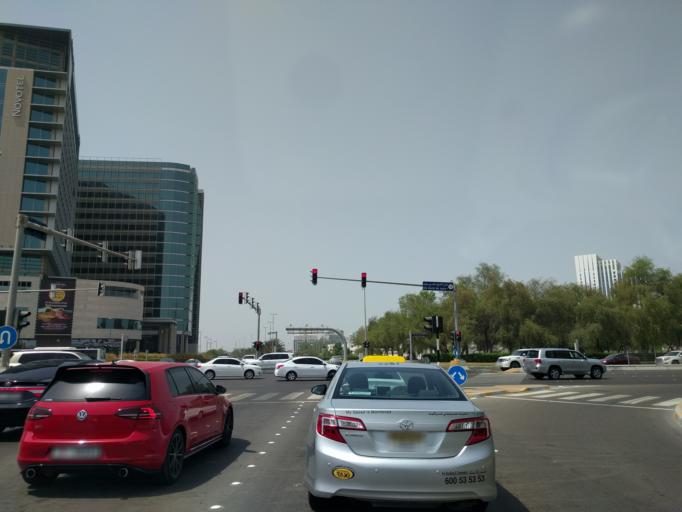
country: AE
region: Abu Dhabi
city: Abu Dhabi
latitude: 24.4286
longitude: 54.4291
